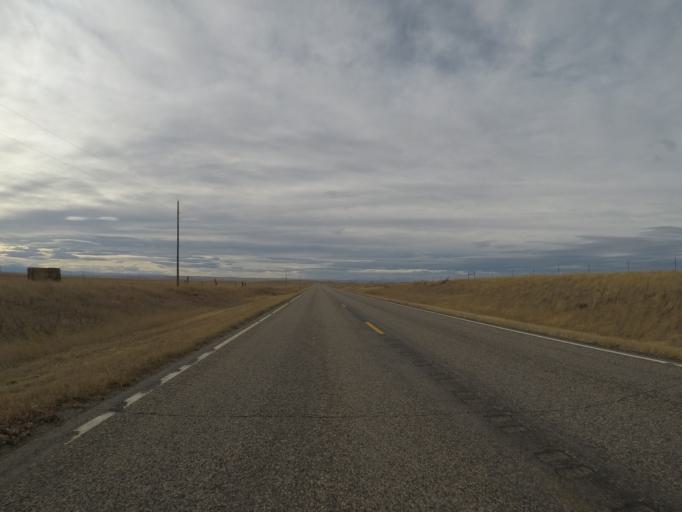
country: US
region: Montana
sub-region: Yellowstone County
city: Laurel
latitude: 45.8566
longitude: -108.8491
